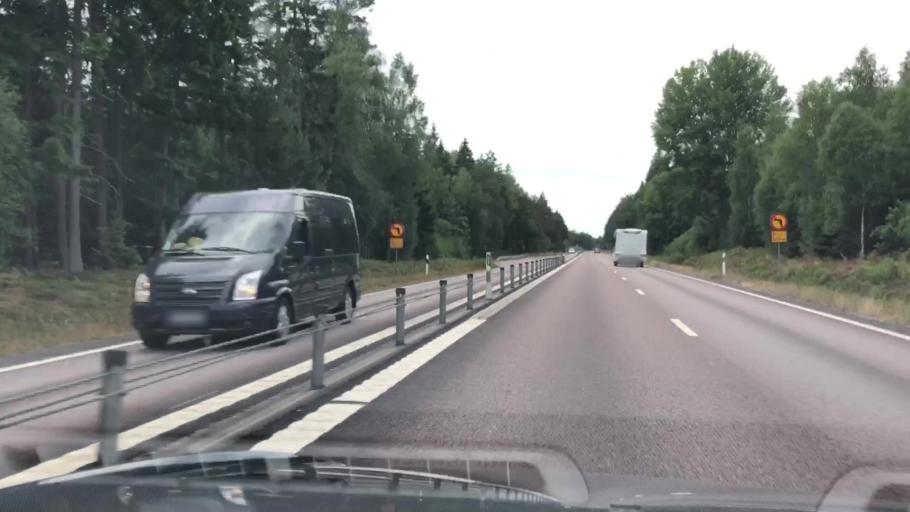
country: SE
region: Blekinge
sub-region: Karlskrona Kommun
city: Jaemjoe
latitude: 56.2491
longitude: 15.9378
